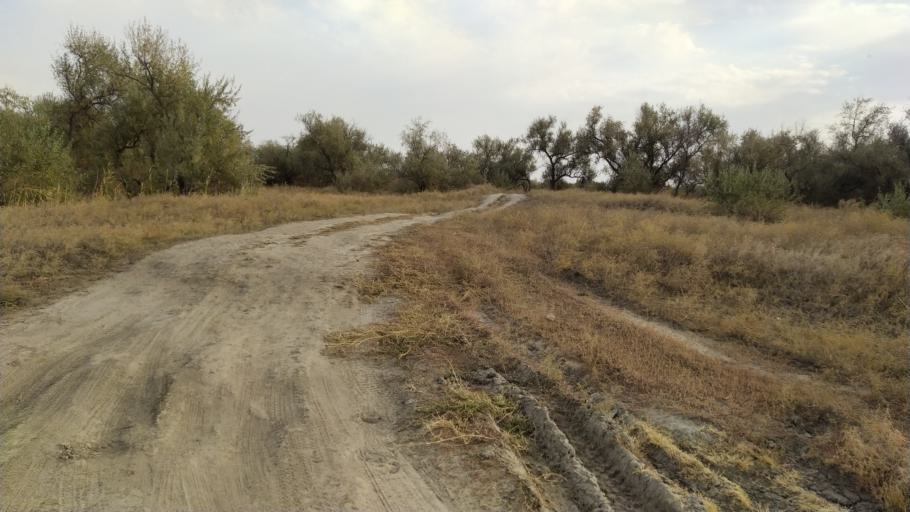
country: RU
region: Rostov
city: Kuleshovka
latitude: 47.1413
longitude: 39.5789
